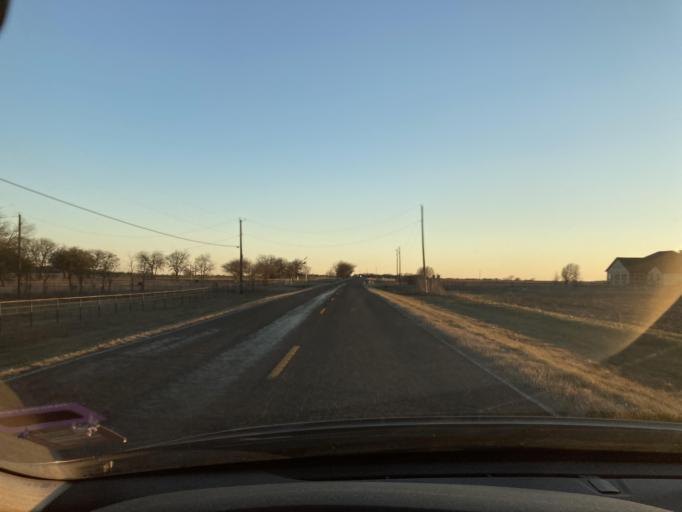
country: US
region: Texas
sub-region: Ellis County
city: Waxahachie
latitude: 32.3306
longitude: -96.8756
